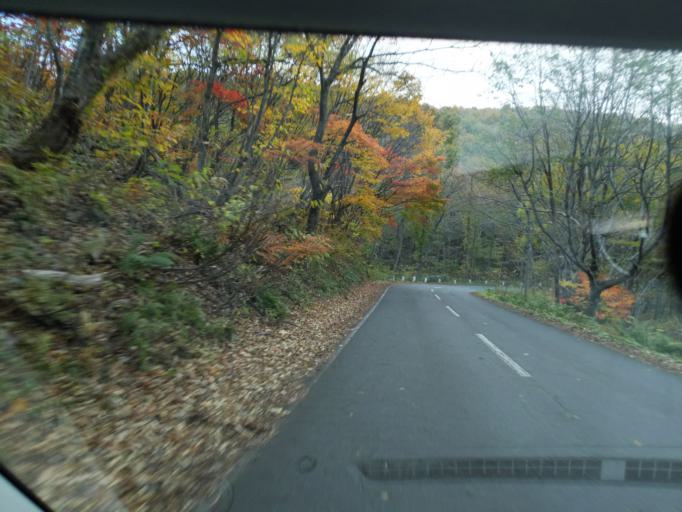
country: JP
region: Iwate
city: Mizusawa
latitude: 39.1158
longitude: 140.8842
